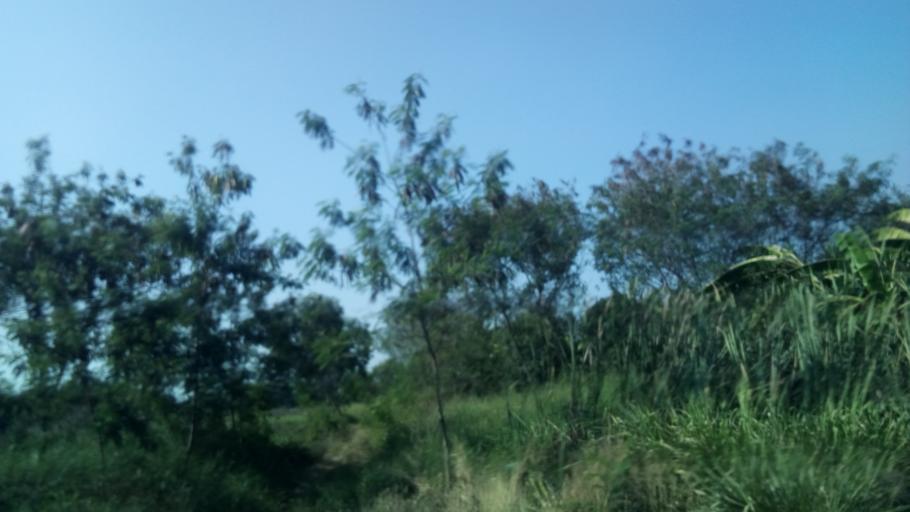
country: TH
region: Nonthaburi
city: Bang Yai
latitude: 13.8810
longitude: 100.3193
